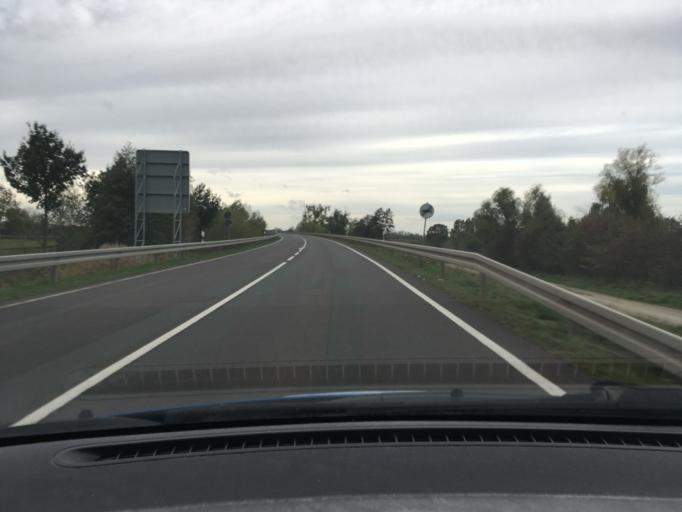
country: DE
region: Saxony-Anhalt
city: Gommern
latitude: 52.0743
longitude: 11.8781
